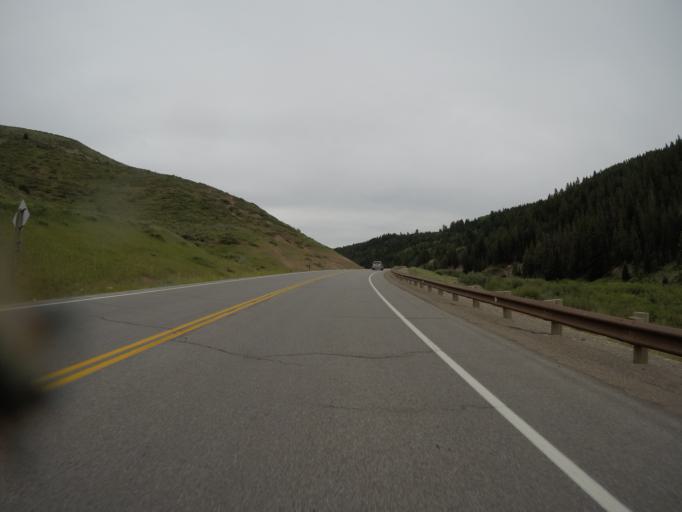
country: US
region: Wyoming
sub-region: Lincoln County
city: Afton
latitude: 42.4877
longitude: -110.9393
